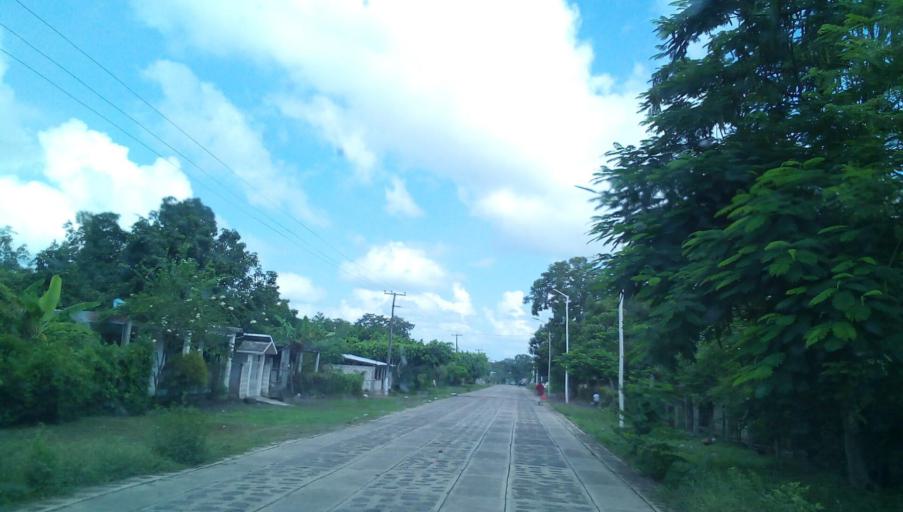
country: MX
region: Veracruz
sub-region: Citlaltepetl
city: Las Sabinas
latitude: 21.3600
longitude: -97.9004
